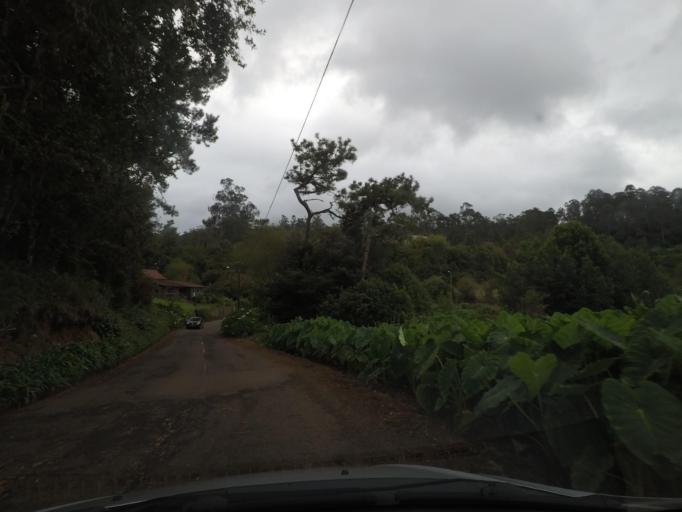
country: PT
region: Madeira
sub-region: Santana
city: Santana
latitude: 32.7846
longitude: -16.8780
